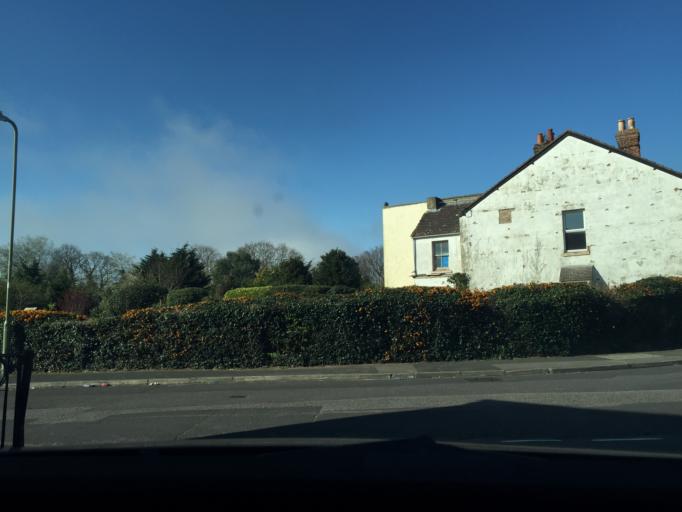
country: GB
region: England
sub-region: Hampshire
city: Gosport
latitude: 50.8065
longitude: -1.1540
